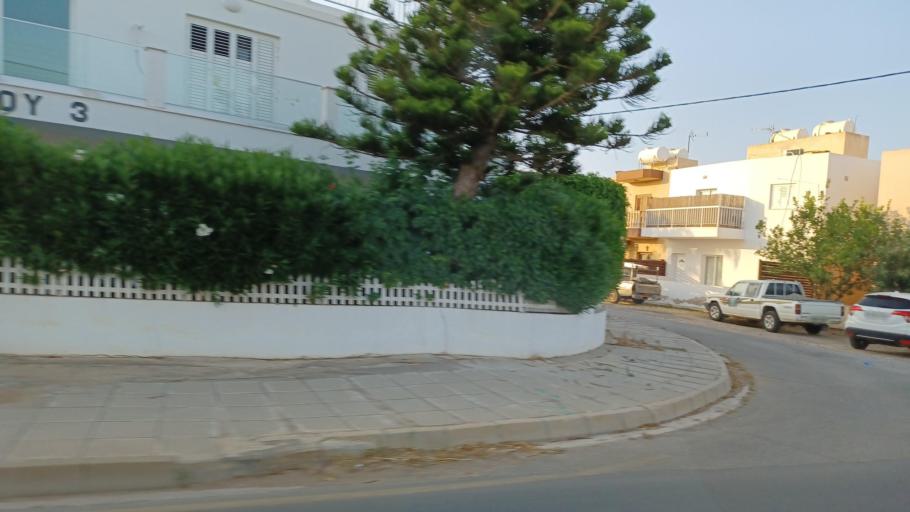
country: CY
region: Ammochostos
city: Frenaros
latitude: 35.0216
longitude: 33.9463
